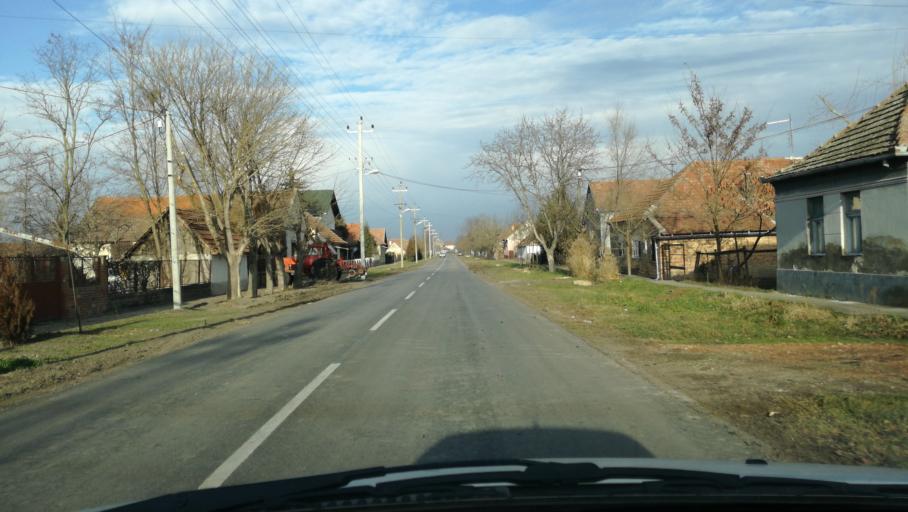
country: RS
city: Rusko Selo
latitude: 45.7638
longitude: 20.5859
